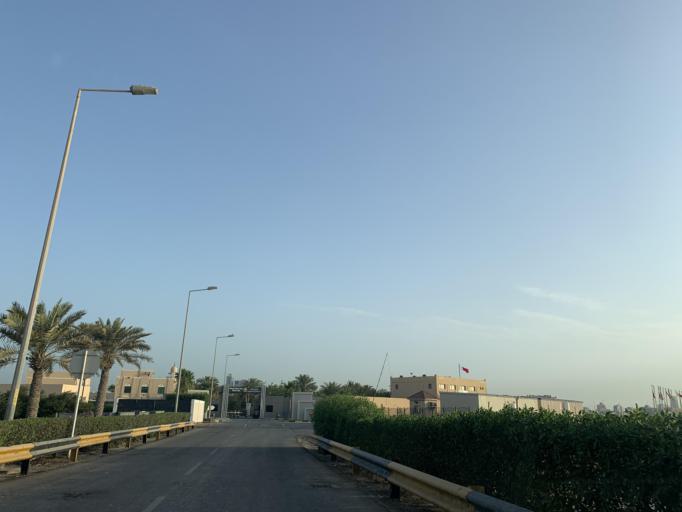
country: BH
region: Manama
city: Manama
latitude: 26.1883
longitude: 50.5854
